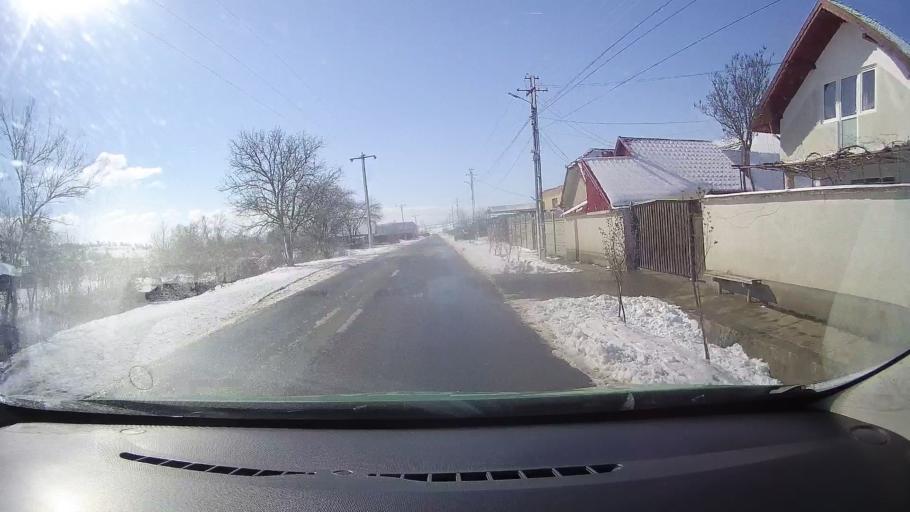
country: RO
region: Sibiu
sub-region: Comuna Vurpar
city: Vurpar
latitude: 45.8892
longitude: 24.3346
